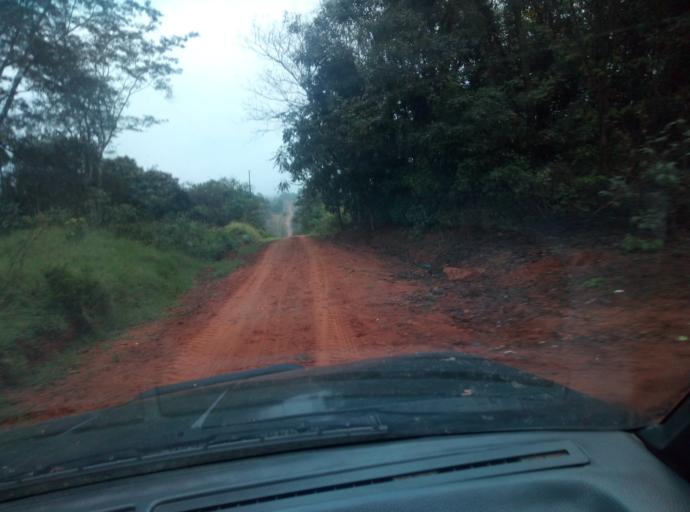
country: PY
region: Caaguazu
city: Carayao
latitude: -25.1903
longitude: -56.3116
